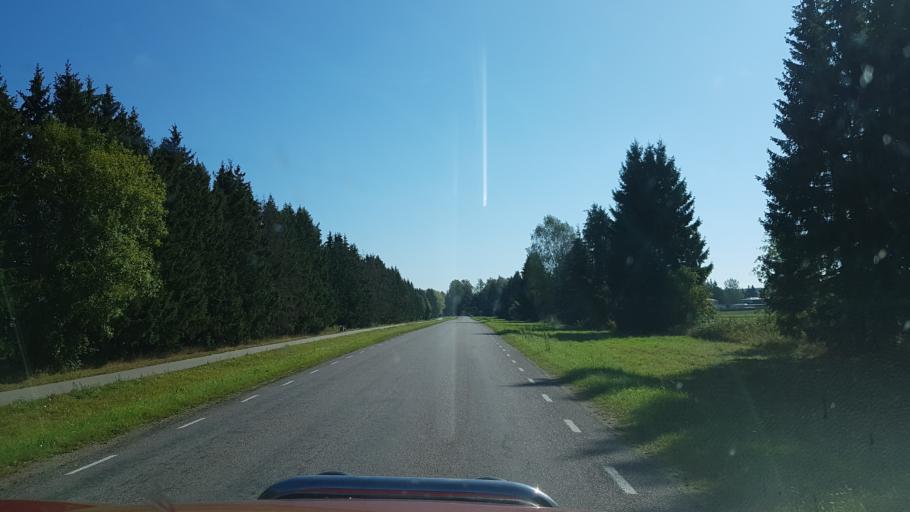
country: EE
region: Tartu
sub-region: Tartu linn
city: Tartu
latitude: 58.3573
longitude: 26.8639
